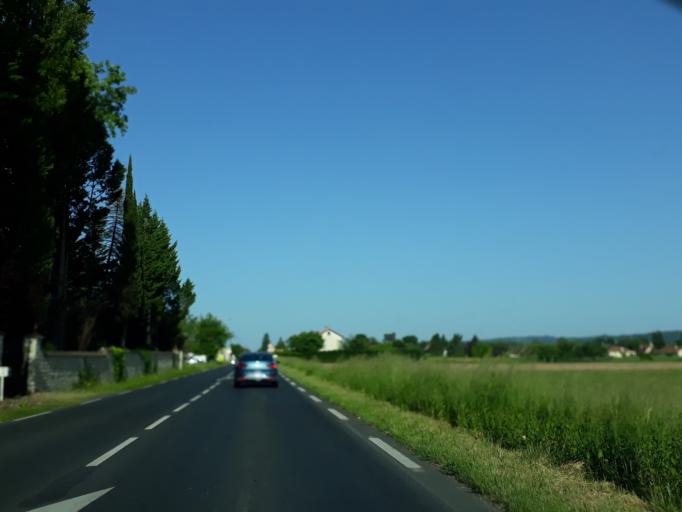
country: FR
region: Limousin
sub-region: Departement de la Correze
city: Larche
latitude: 45.1258
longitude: 1.3870
